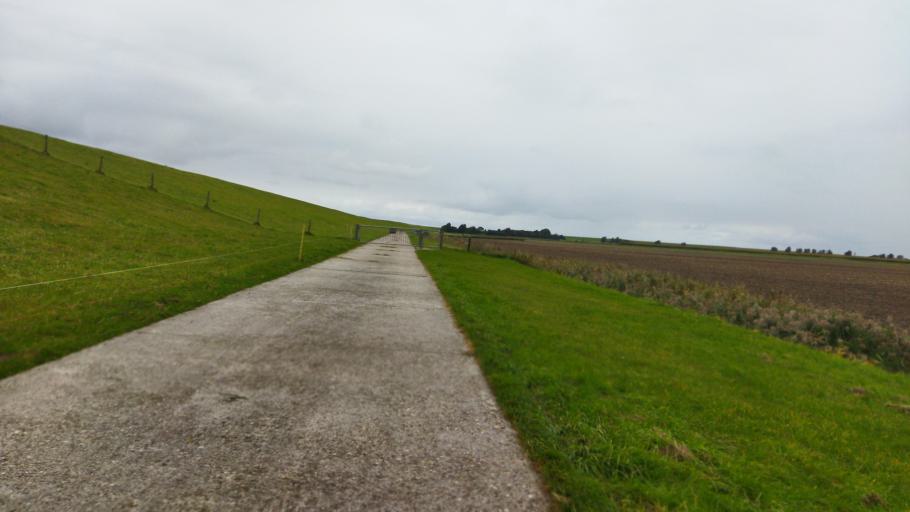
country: DE
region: Lower Saxony
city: Hinte
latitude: 53.4746
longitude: 7.0323
